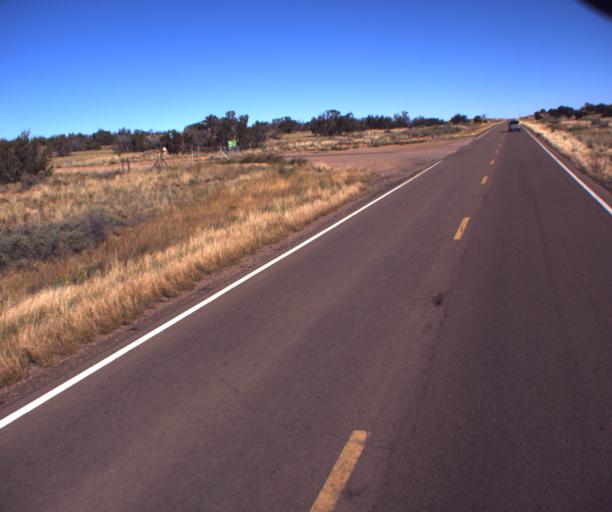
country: US
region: Arizona
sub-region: Navajo County
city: Snowflake
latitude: 34.6147
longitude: -110.0910
